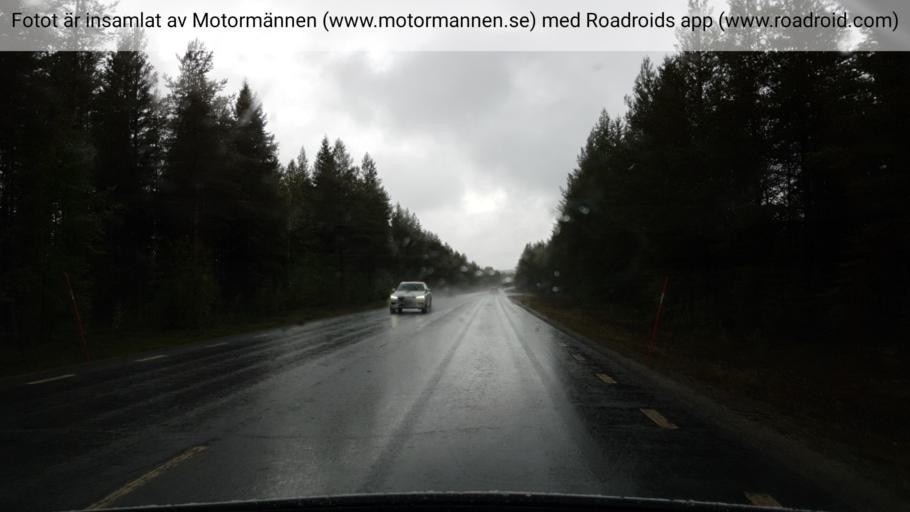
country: SE
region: Vaesterbotten
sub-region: Vindelns Kommun
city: Vindeln
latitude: 64.1425
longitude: 19.8980
